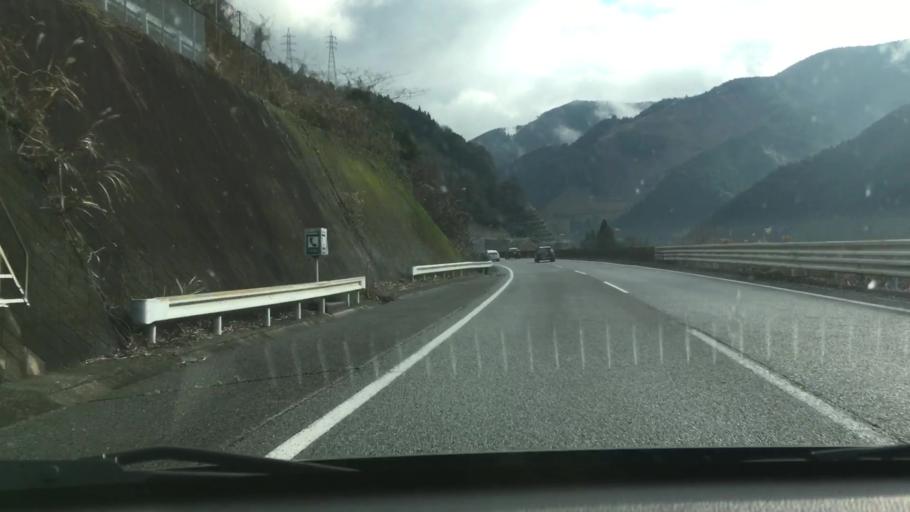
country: JP
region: Kumamoto
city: Yatsushiro
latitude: 32.4083
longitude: 130.6969
